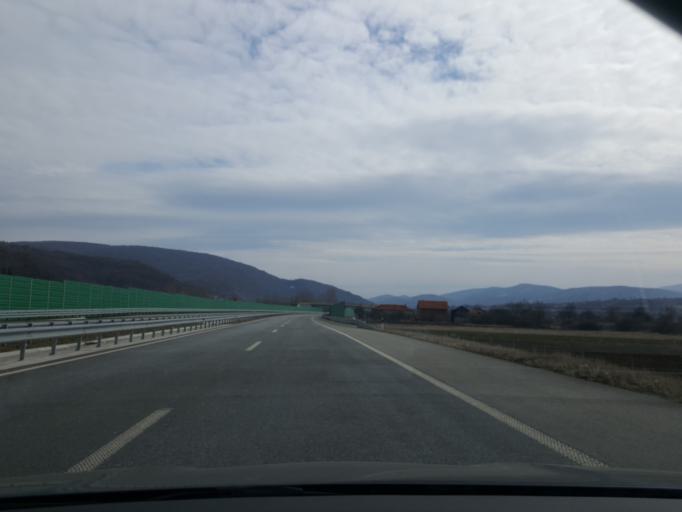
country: RS
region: Central Serbia
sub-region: Pirotski Okrug
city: Dimitrovgrad
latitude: 43.0488
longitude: 22.7024
